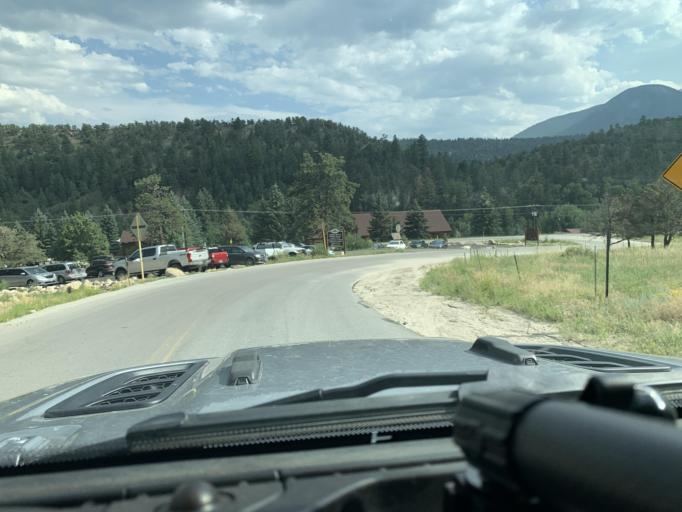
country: US
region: Colorado
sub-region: Chaffee County
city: Buena Vista
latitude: 38.7339
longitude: -106.1641
